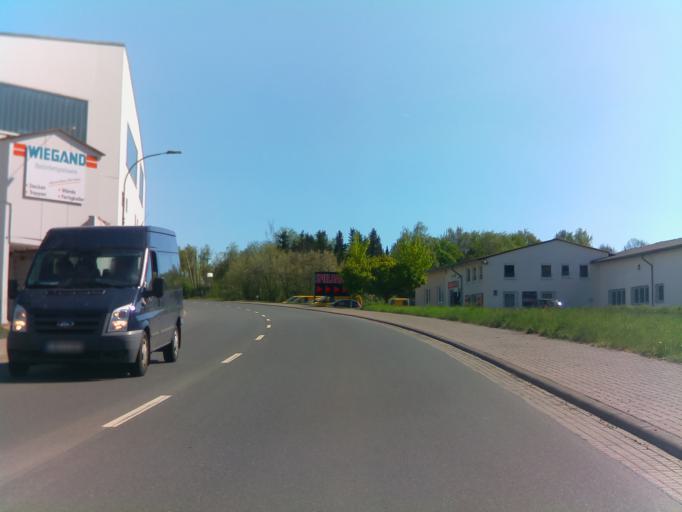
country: DE
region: Hesse
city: Herbstein
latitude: 50.5550
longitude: 9.3522
